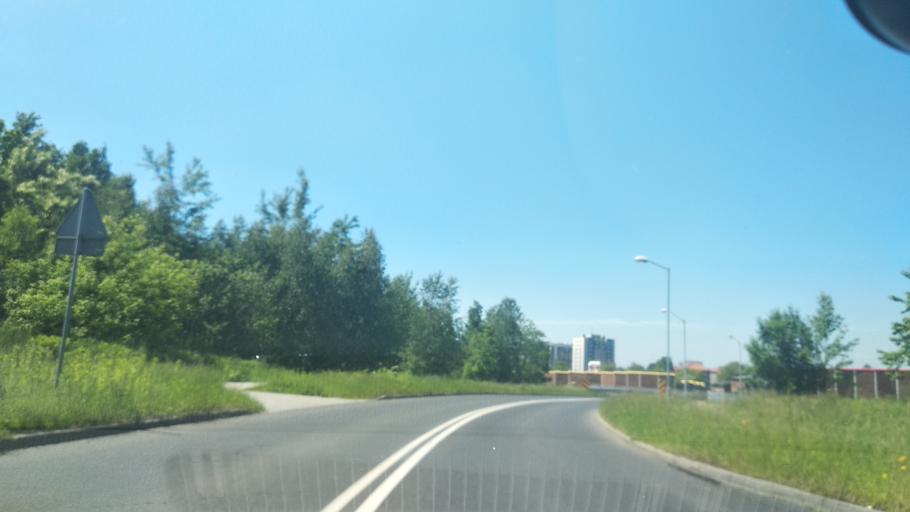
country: PL
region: Silesian Voivodeship
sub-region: Swietochlowice
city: Swietochlowice
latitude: 50.2496
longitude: 18.9178
